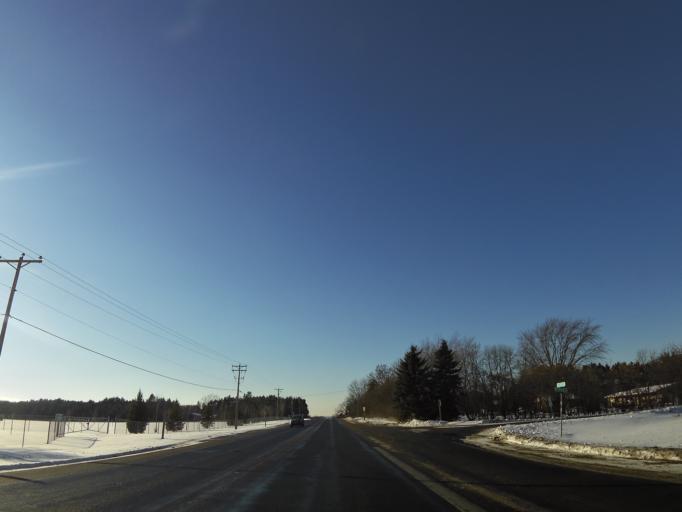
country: US
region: Wisconsin
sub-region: Saint Croix County
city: Hudson
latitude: 44.9781
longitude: -92.6920
